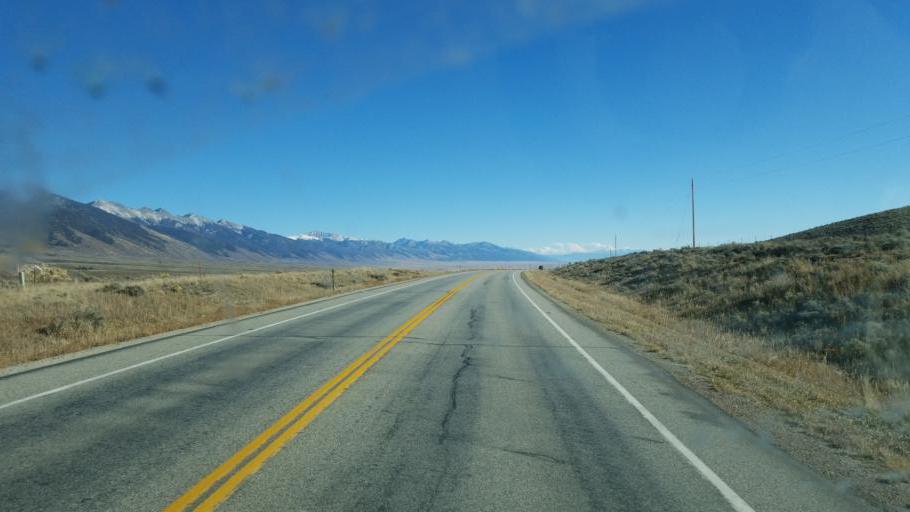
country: US
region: Colorado
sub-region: Chaffee County
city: Salida
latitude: 38.3927
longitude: -106.0597
